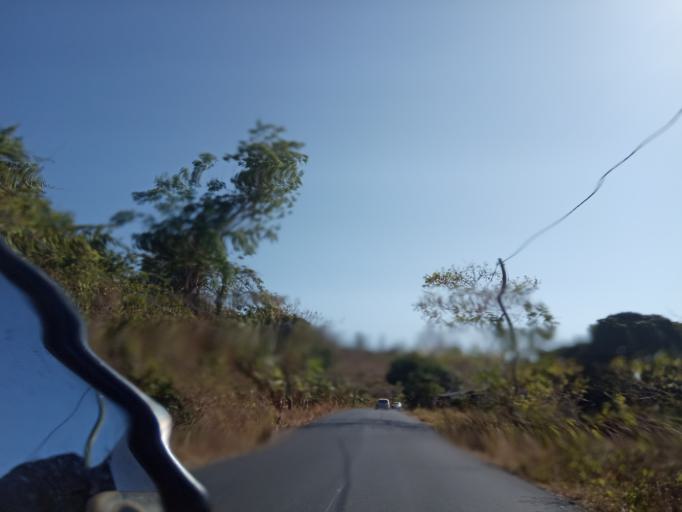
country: YT
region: Bandrele
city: Bandrele
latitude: -12.8880
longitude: 45.2115
